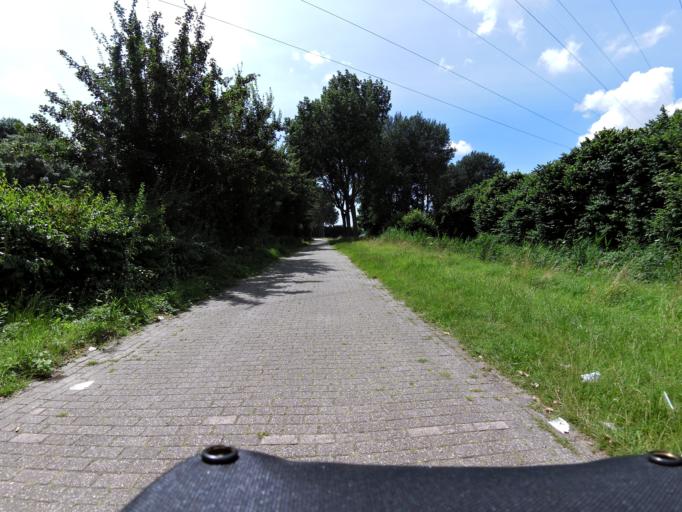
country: NL
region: South Holland
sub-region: Gemeente Albrandswaard
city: Rhoon
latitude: 51.8675
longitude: 4.4364
